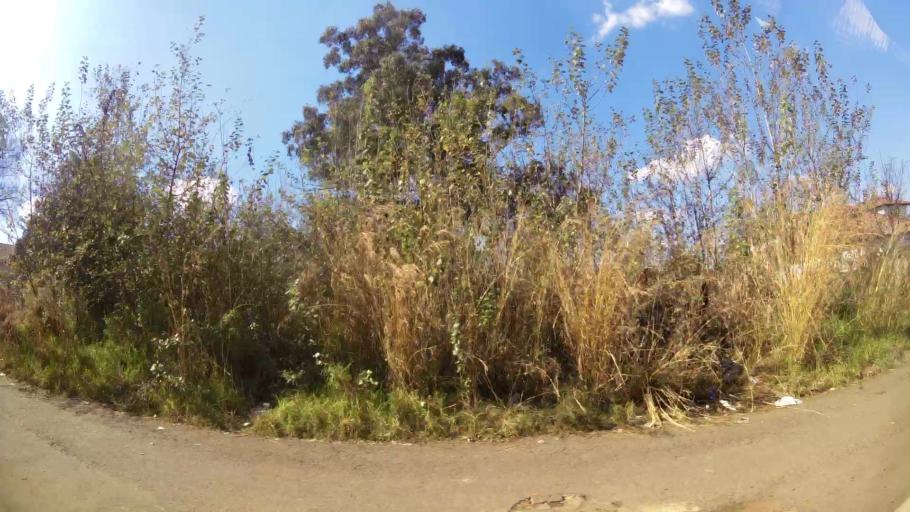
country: ZA
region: Mpumalanga
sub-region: Nkangala District Municipality
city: Witbank
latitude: -25.9292
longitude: 29.2368
